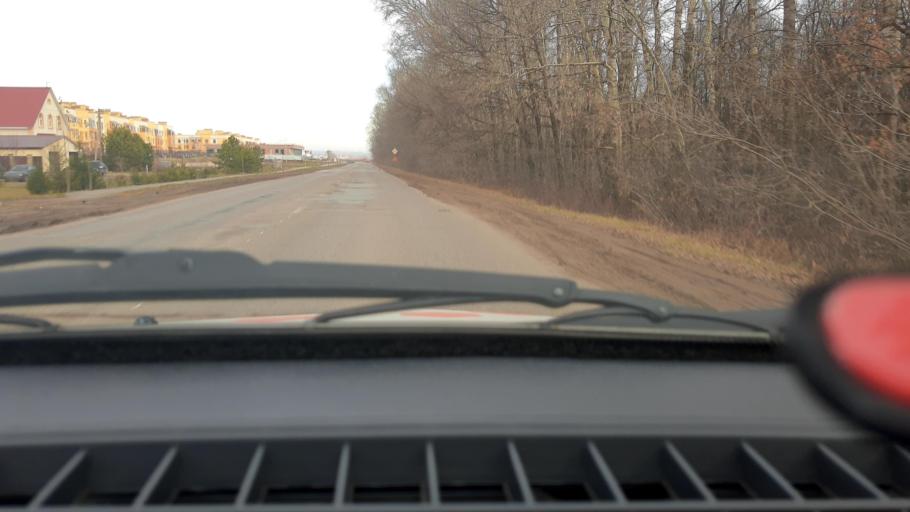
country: RU
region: Bashkortostan
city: Ufa
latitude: 54.7930
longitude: 55.9569
